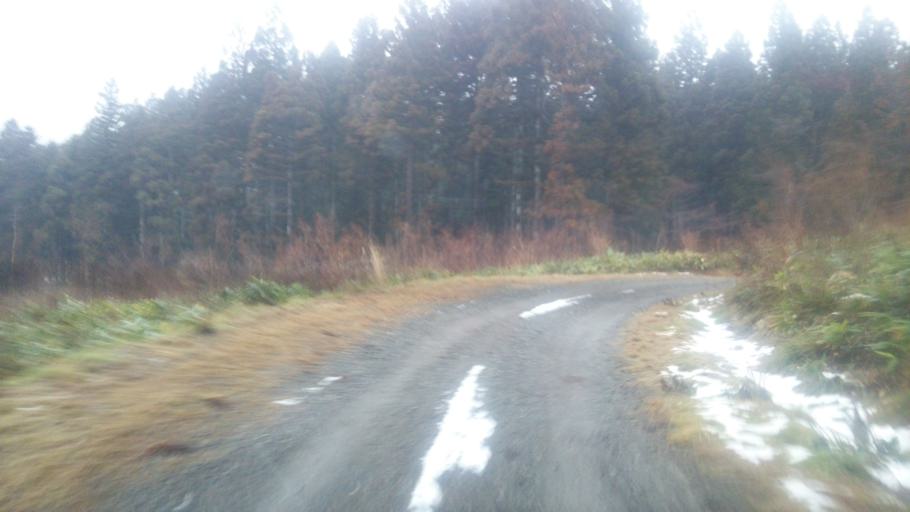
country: JP
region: Fukushima
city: Kitakata
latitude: 37.5772
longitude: 139.9786
